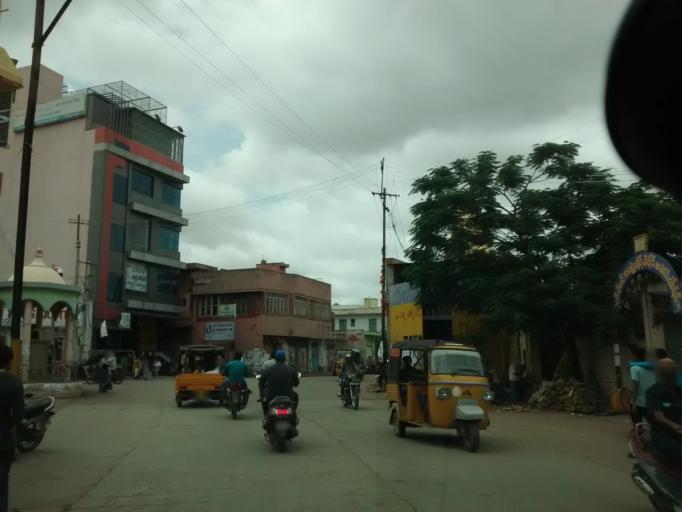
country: IN
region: Andhra Pradesh
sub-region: Anantapur
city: Hindupur
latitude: 13.8251
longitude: 77.4894
